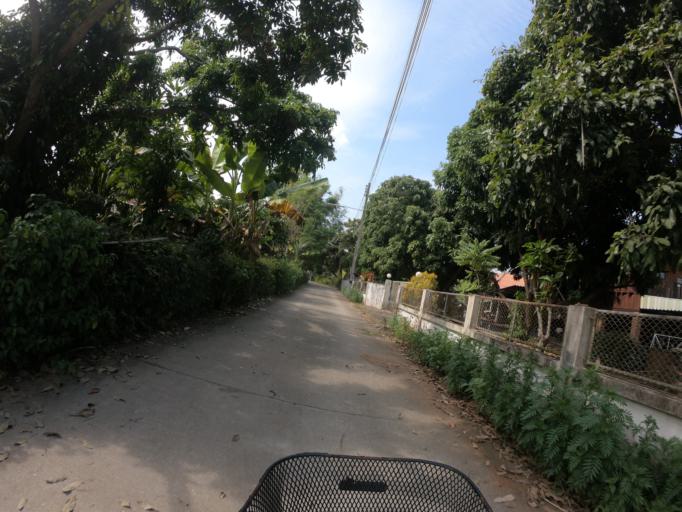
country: TH
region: Chiang Mai
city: Saraphi
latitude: 18.7100
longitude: 99.0213
